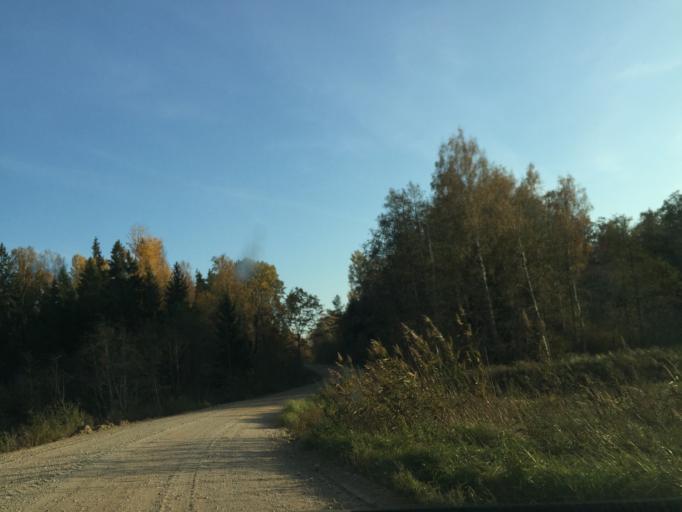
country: LV
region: Vainode
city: Vainode
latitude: 56.5940
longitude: 21.8355
